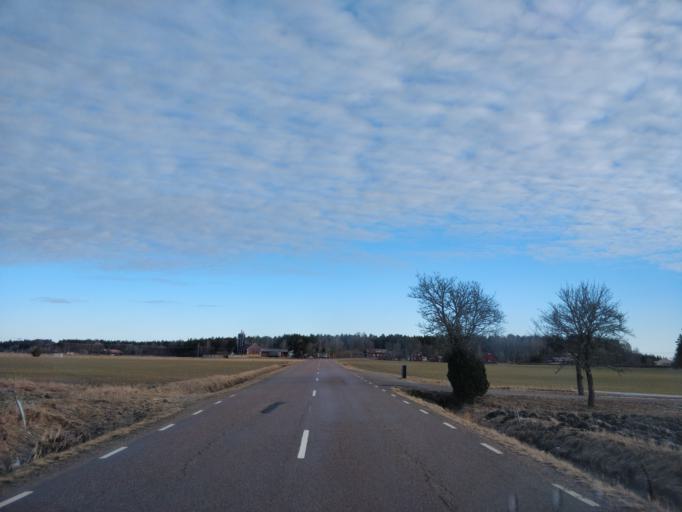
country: SE
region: Uppsala
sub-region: Enkopings Kommun
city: Enkoping
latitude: 59.8088
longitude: 17.1006
